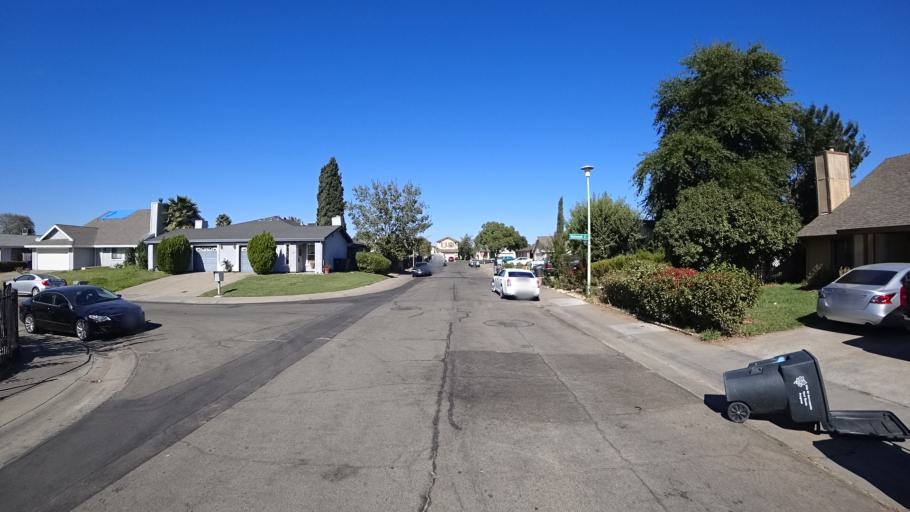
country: US
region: California
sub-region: Sacramento County
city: Florin
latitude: 38.4807
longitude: -121.4323
